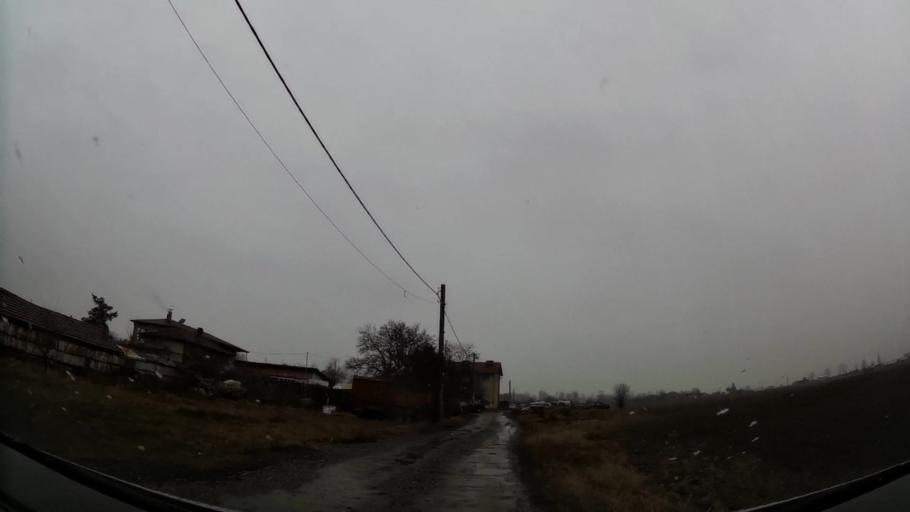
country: BG
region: Sofia-Capital
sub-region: Stolichna Obshtina
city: Sofia
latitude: 42.6659
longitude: 23.4273
